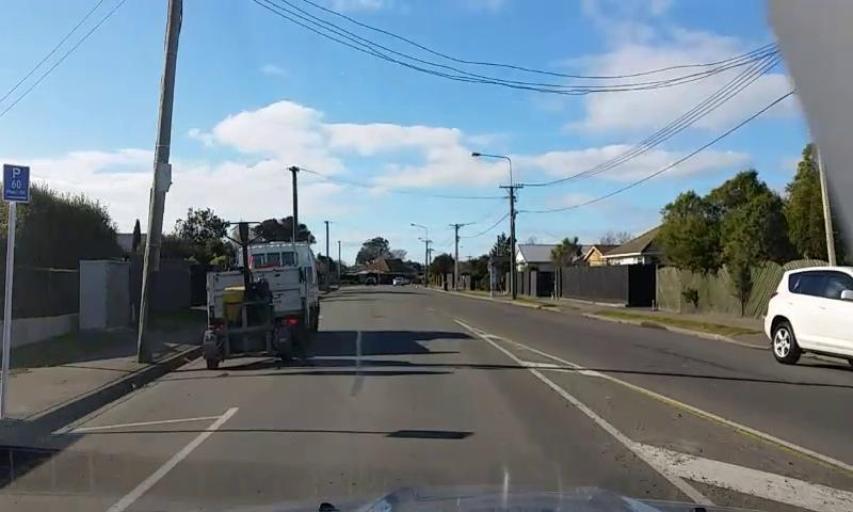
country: NZ
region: Canterbury
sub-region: Christchurch City
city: Christchurch
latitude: -43.4952
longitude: 172.7112
